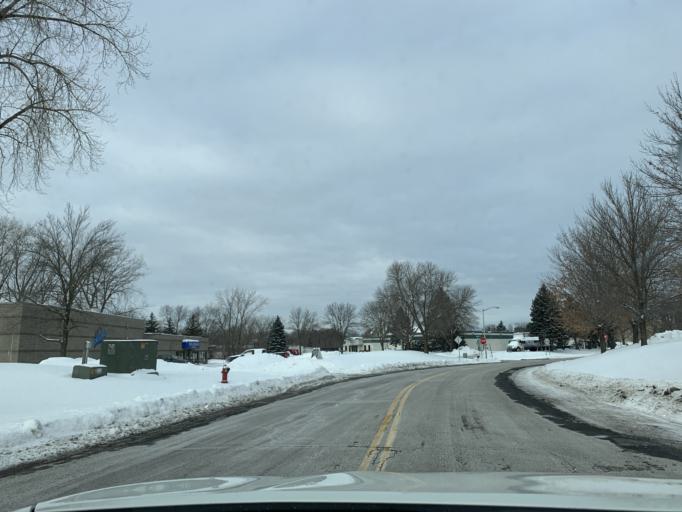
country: US
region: Minnesota
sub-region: Hennepin County
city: West Coon Rapids
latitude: 45.1770
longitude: -93.2974
